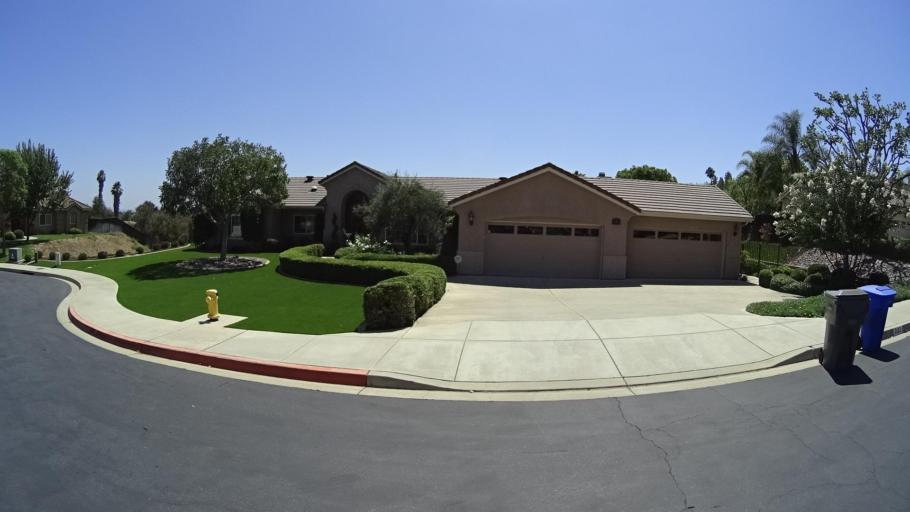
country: US
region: California
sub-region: San Diego County
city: Fallbrook
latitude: 33.3644
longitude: -117.2523
